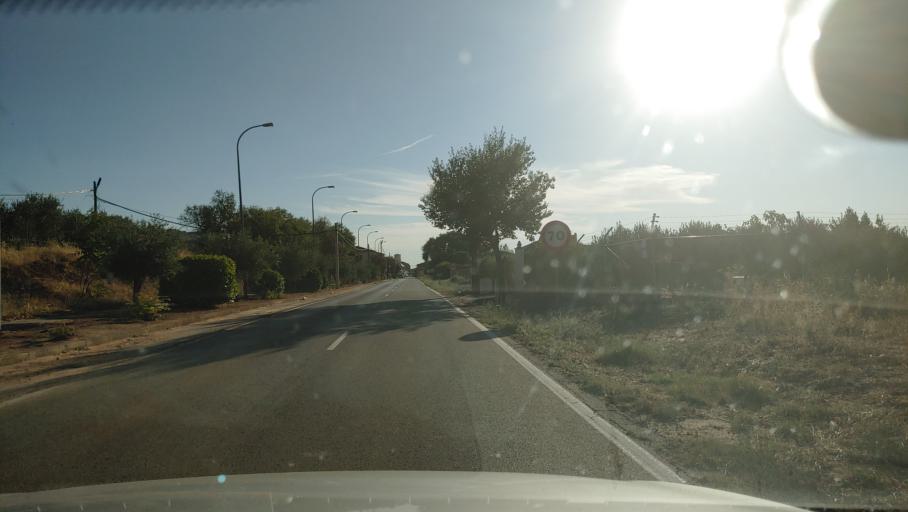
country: ES
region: Castille-La Mancha
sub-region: Provincia de Ciudad Real
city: Infantes
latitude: 38.7421
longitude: -3.0025
